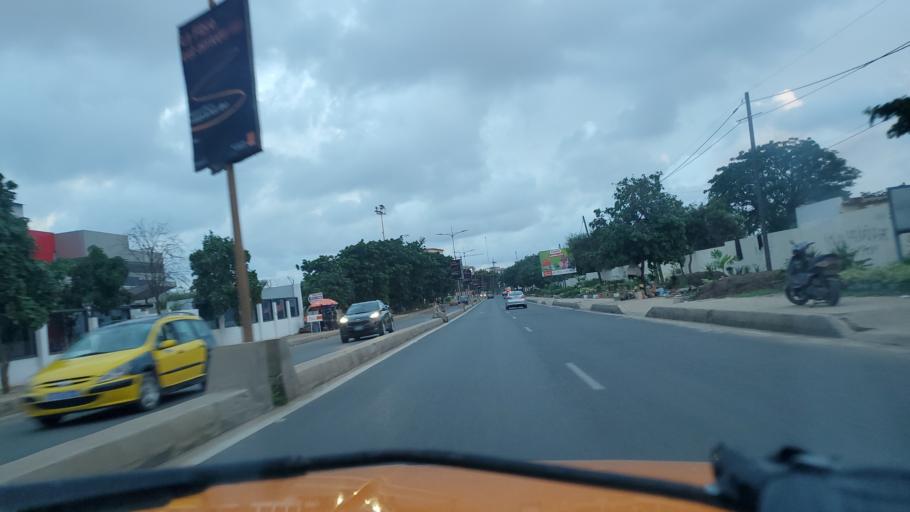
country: SN
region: Dakar
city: Mermoz Boabab
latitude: 14.7078
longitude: -17.4804
